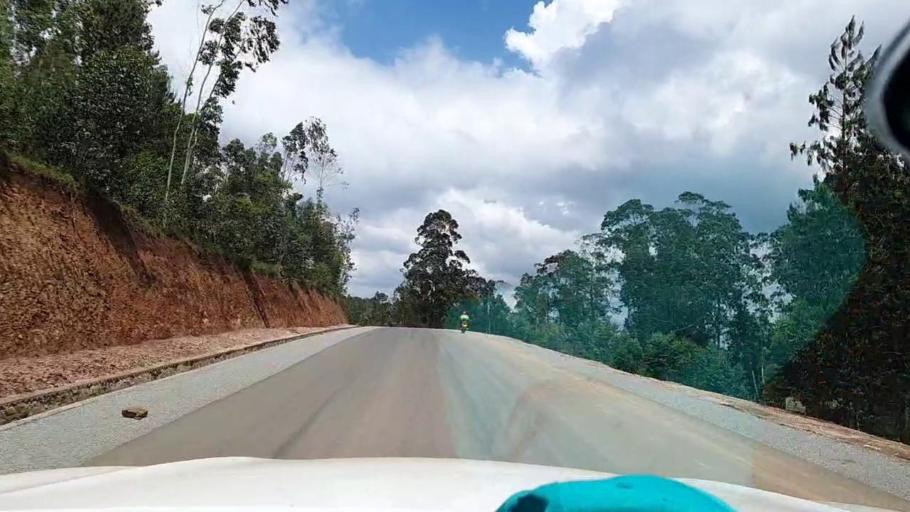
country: RW
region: Southern Province
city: Nzega
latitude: -2.6424
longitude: 29.5799
